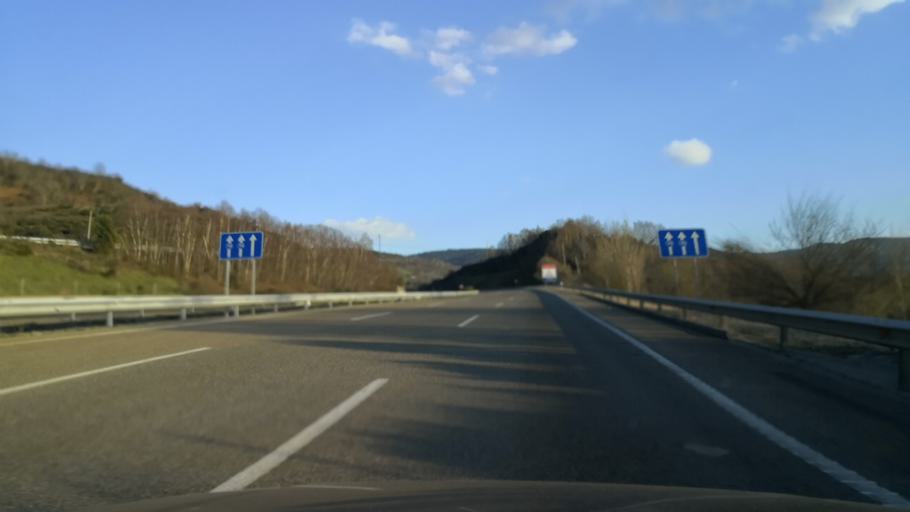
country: ES
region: Galicia
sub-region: Provincia de Lugo
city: San Roman
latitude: 42.7472
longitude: -7.0565
